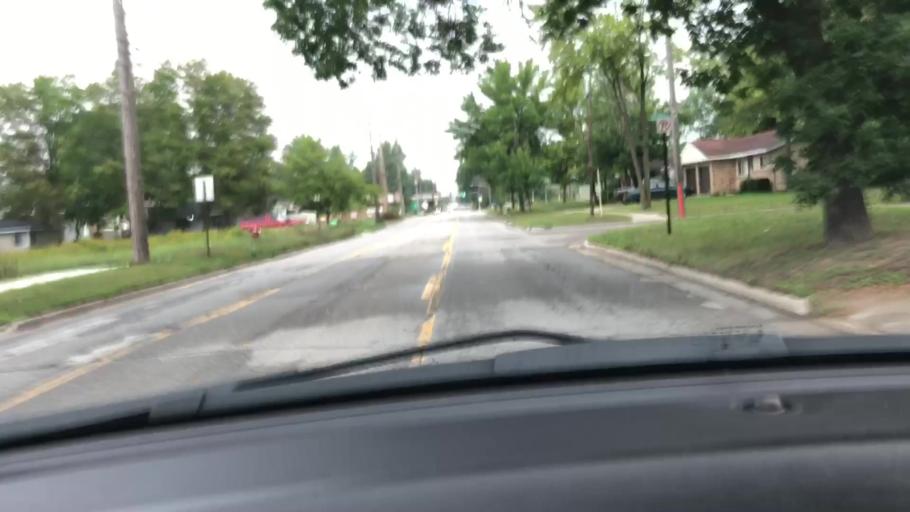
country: US
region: Michigan
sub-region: Midland County
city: Midland
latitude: 43.6078
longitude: -84.1875
